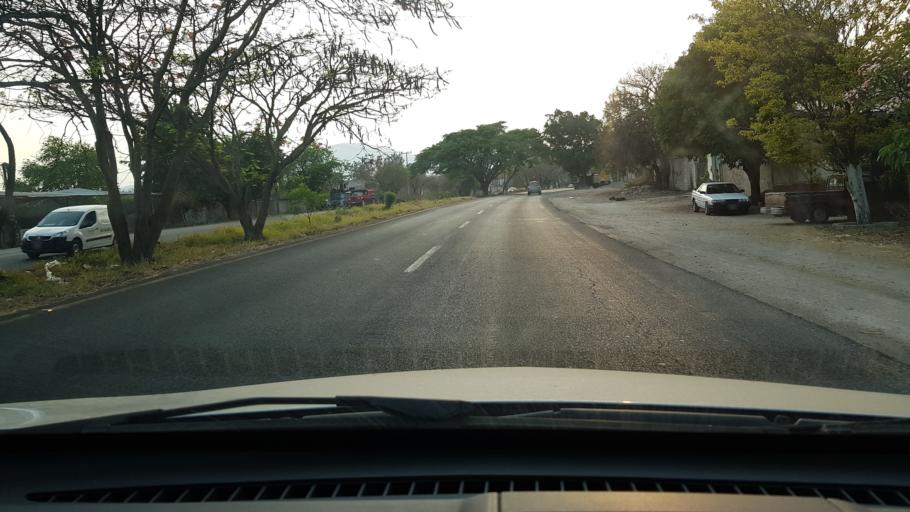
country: MX
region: Morelos
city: Yautepec
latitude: 18.8703
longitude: -99.0635
